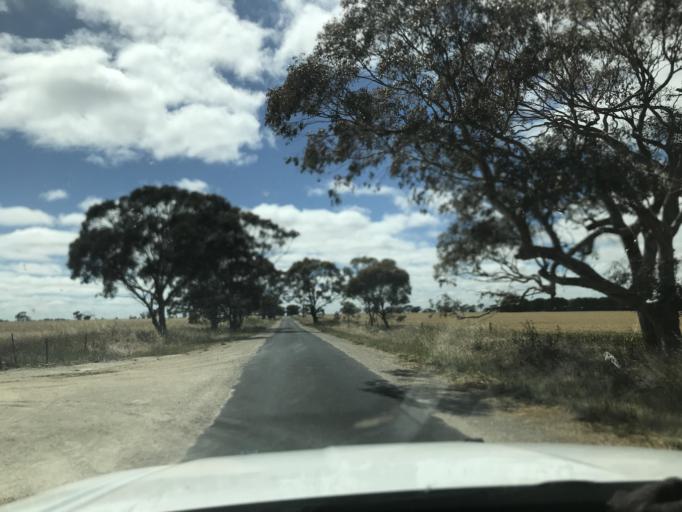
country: AU
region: South Australia
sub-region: Tatiara
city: Bordertown
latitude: -36.2786
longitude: 141.1169
